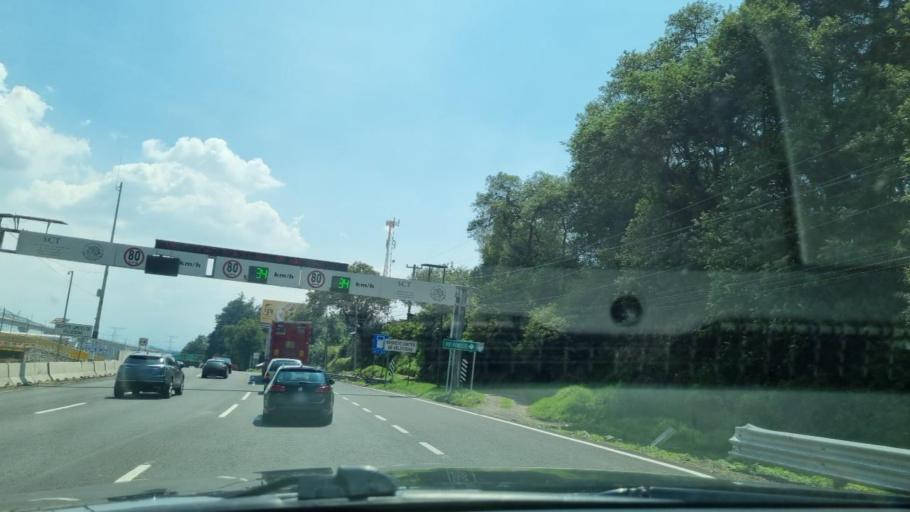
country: MX
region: Mexico
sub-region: Lerma
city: San Miguel Ameyalco
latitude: 19.2924
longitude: -99.4314
